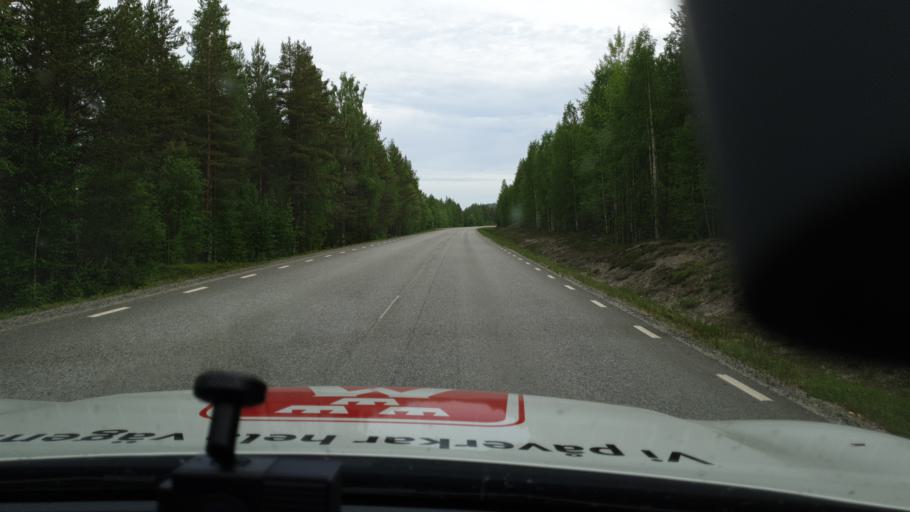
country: SE
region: Vaesterbotten
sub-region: Lycksele Kommun
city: Lycksele
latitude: 64.6230
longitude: 18.6842
